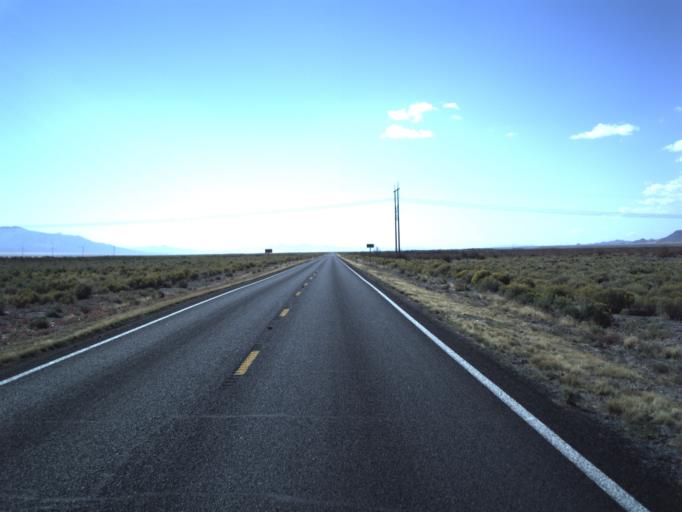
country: US
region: Utah
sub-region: Beaver County
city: Milford
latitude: 38.5758
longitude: -112.9896
